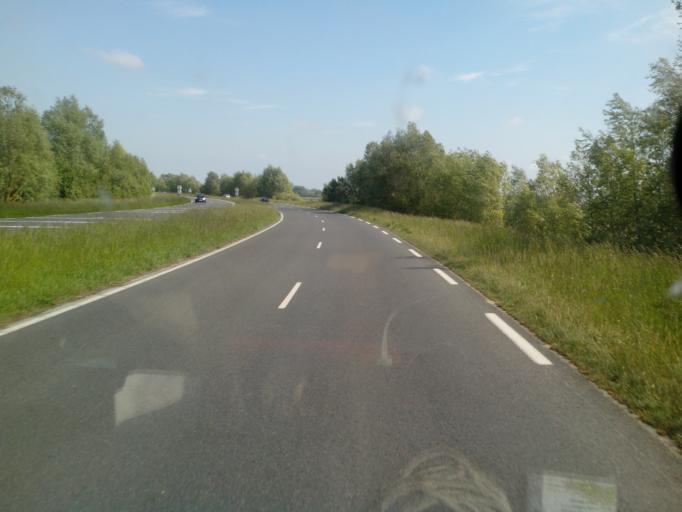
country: FR
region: Picardie
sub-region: Departement de la Somme
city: Quend
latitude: 50.3061
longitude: 1.6366
